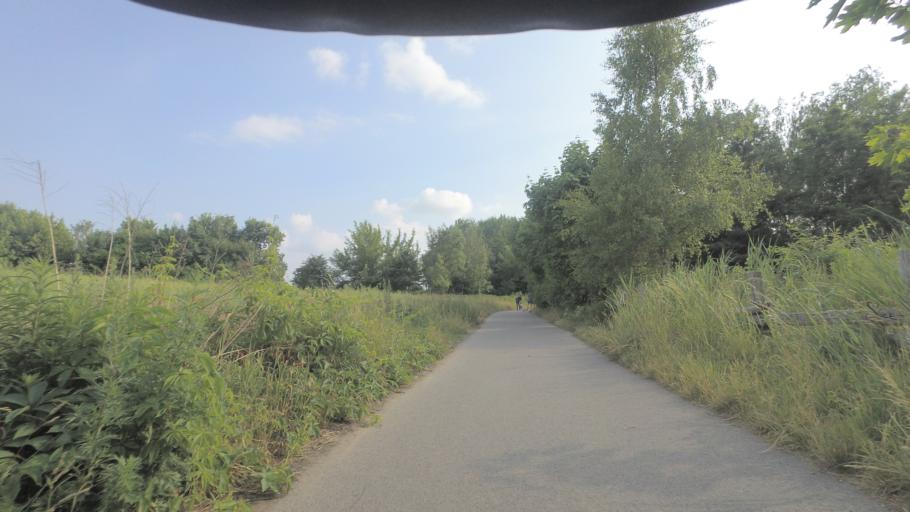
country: DE
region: Berlin
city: Lichtenrade
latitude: 52.3864
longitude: 13.4277
